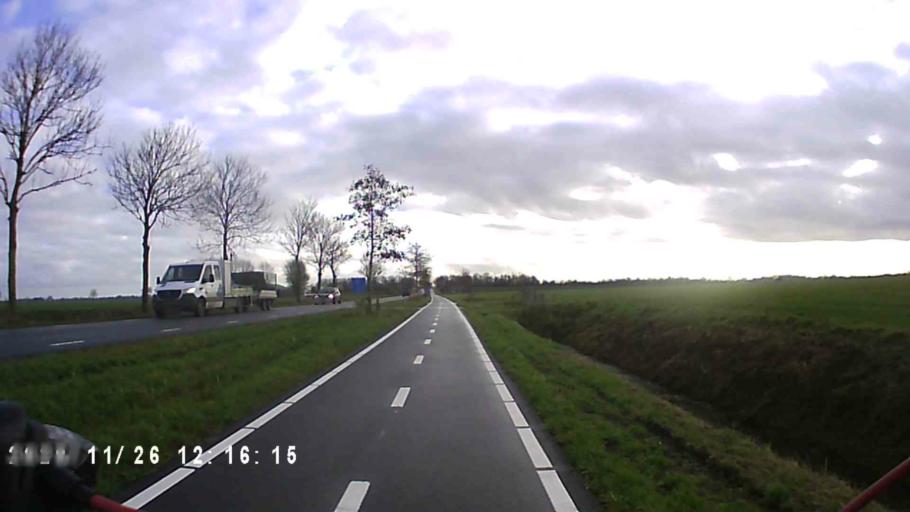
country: NL
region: Groningen
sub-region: Gemeente Bedum
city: Bedum
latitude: 53.3368
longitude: 6.6646
